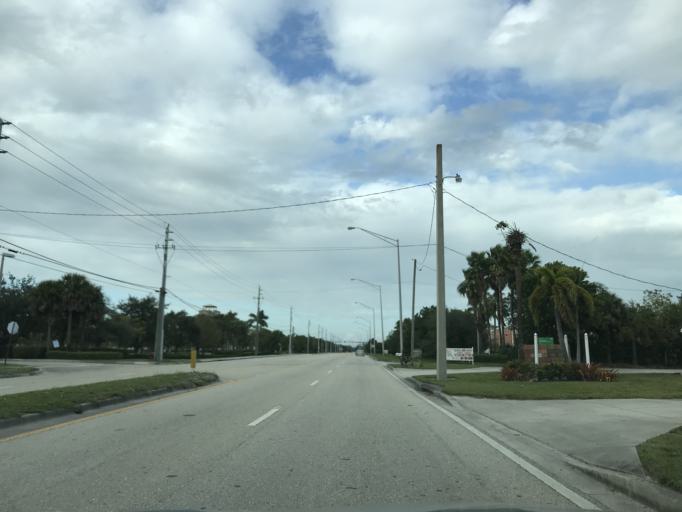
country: US
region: Florida
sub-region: Palm Beach County
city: Lake Belvedere Estates
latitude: 26.6821
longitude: -80.1657
